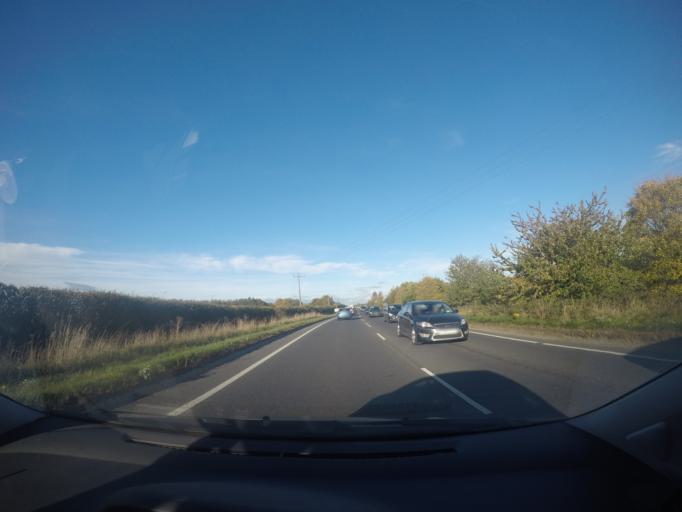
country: GB
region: England
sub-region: City of York
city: Nether Poppleton
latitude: 53.9639
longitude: -1.1498
